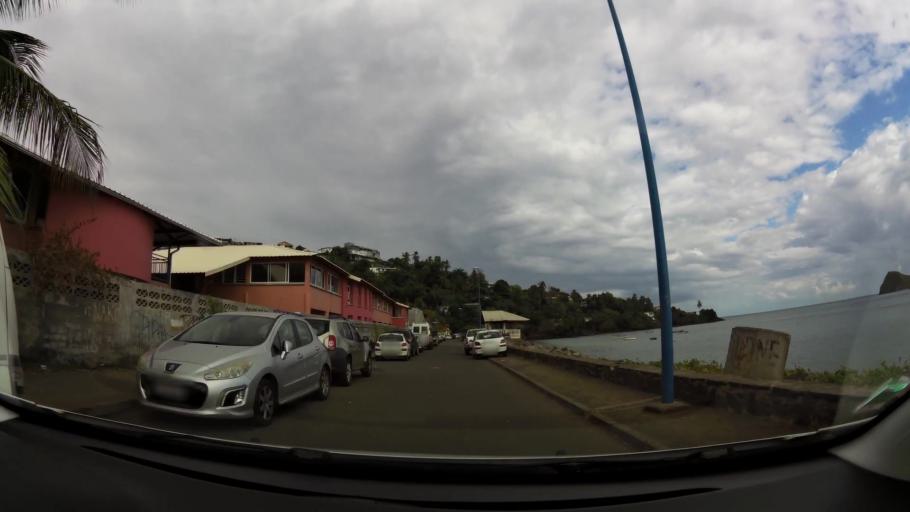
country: YT
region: Sada
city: Sada
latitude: -12.8502
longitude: 45.0979
